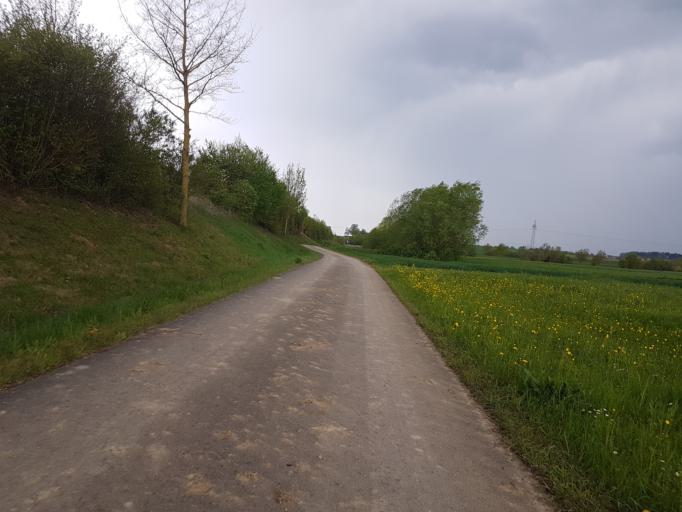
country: DE
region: Baden-Wuerttemberg
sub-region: Regierungsbezirk Stuttgart
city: Bondorf
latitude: 48.5065
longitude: 8.8048
